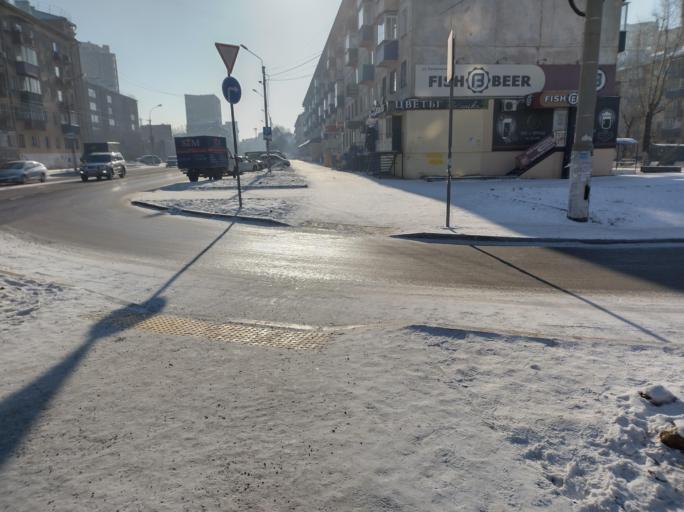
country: RU
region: Transbaikal Territory
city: Chita
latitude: 52.0359
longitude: 113.4901
